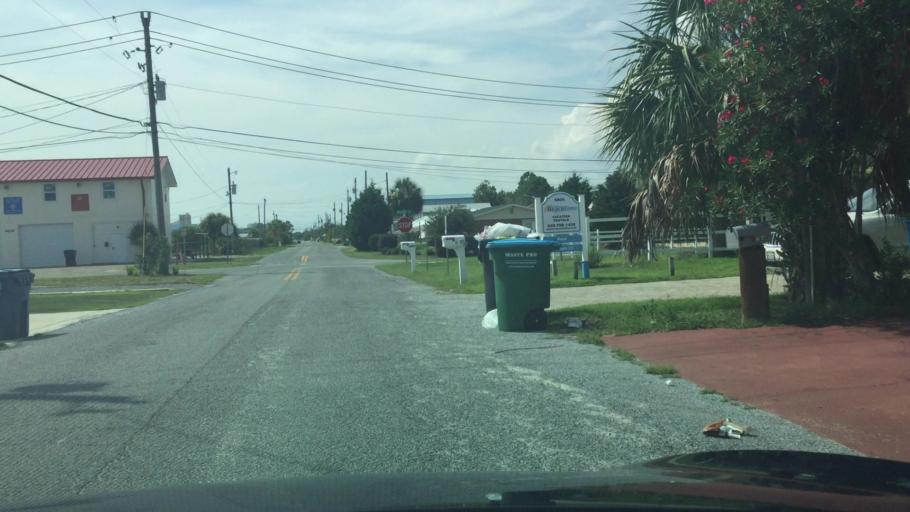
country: US
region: Florida
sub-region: Bay County
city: Lower Grand Lagoon
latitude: 30.1559
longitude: -85.7696
